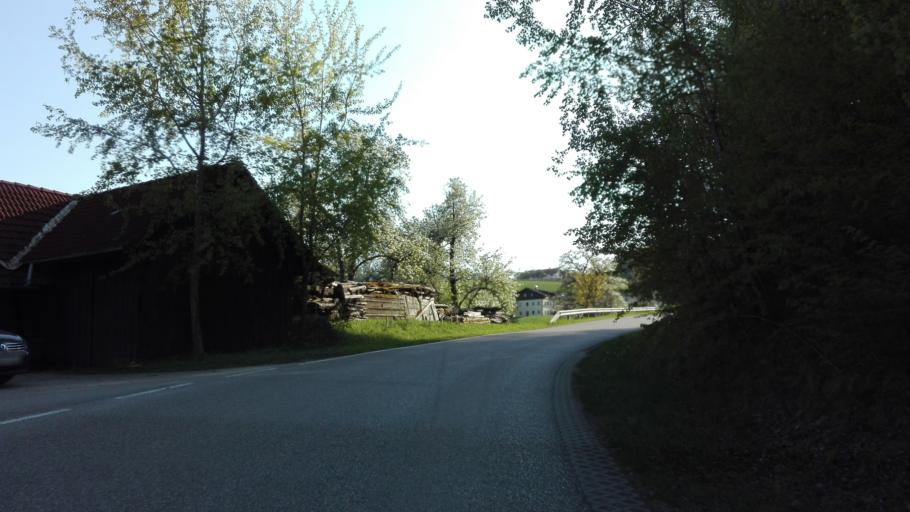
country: AT
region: Upper Austria
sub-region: Politischer Bezirk Grieskirchen
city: Grieskirchen
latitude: 48.3639
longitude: 13.7883
